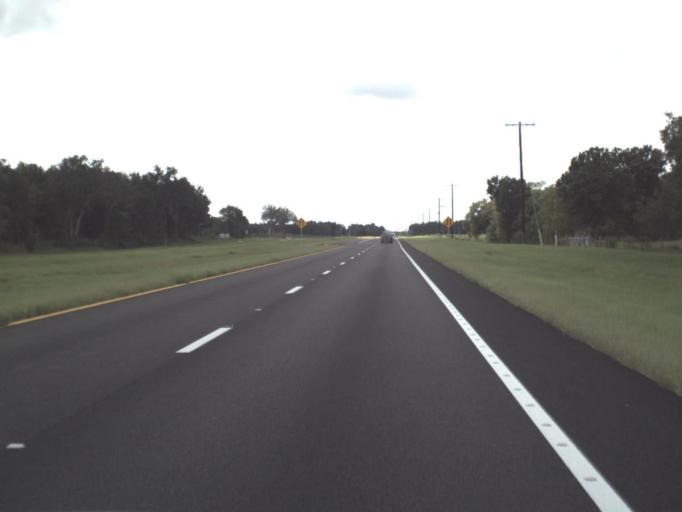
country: US
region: Florida
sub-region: Hardee County
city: Zolfo Springs
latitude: 27.4148
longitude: -81.7956
